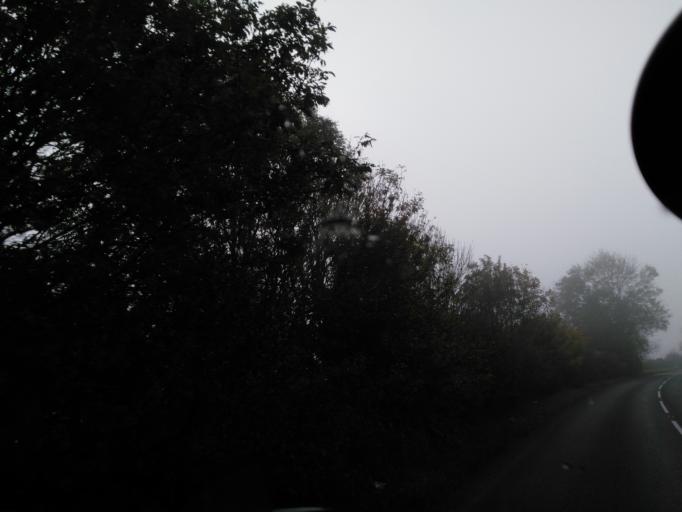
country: GB
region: England
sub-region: Wiltshire
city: Atworth
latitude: 51.4081
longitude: -2.1650
